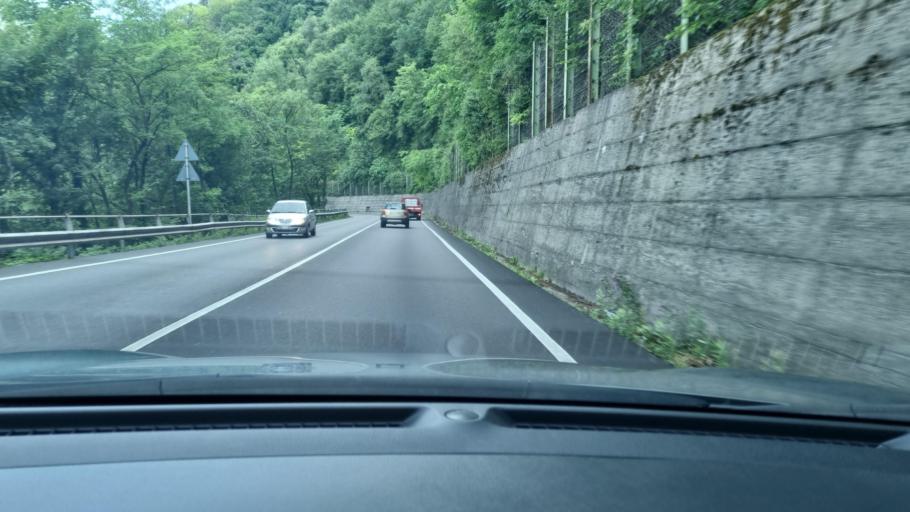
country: IT
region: Lombardy
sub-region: Provincia di Bergamo
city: Ubiale
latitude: 45.7721
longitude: 9.6144
